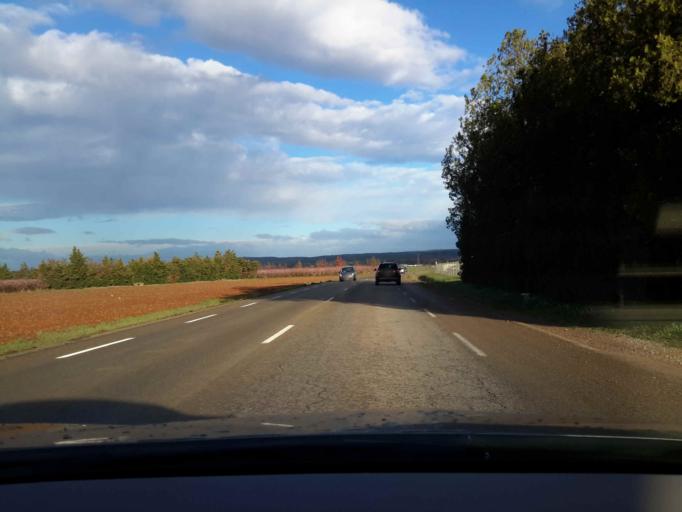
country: FR
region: Languedoc-Roussillon
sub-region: Departement du Gard
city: Aubord
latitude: 43.7585
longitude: 4.3386
